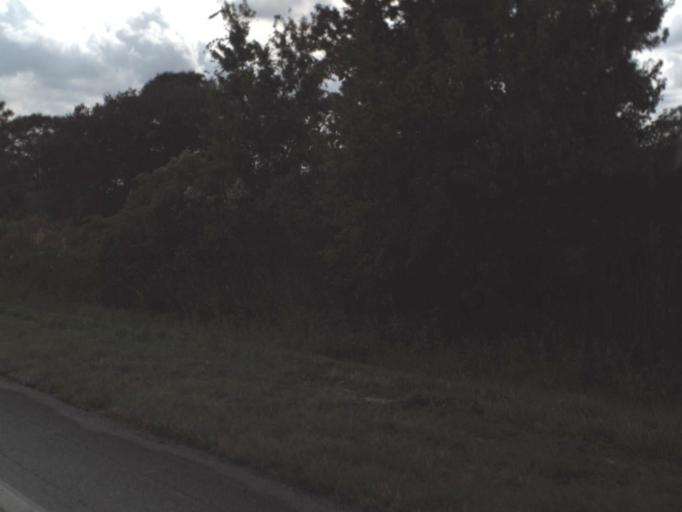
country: US
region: Florida
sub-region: Okeechobee County
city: Cypress Quarters
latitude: 27.4975
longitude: -80.8058
